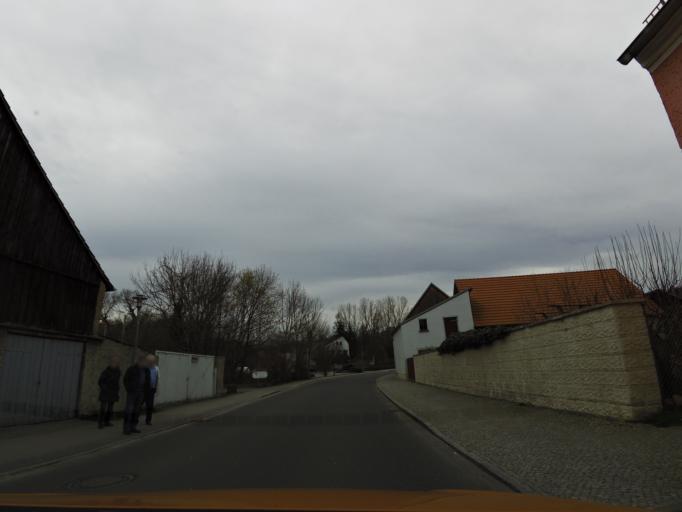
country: DE
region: Brandenburg
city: Belzig
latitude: 52.1389
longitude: 12.5896
